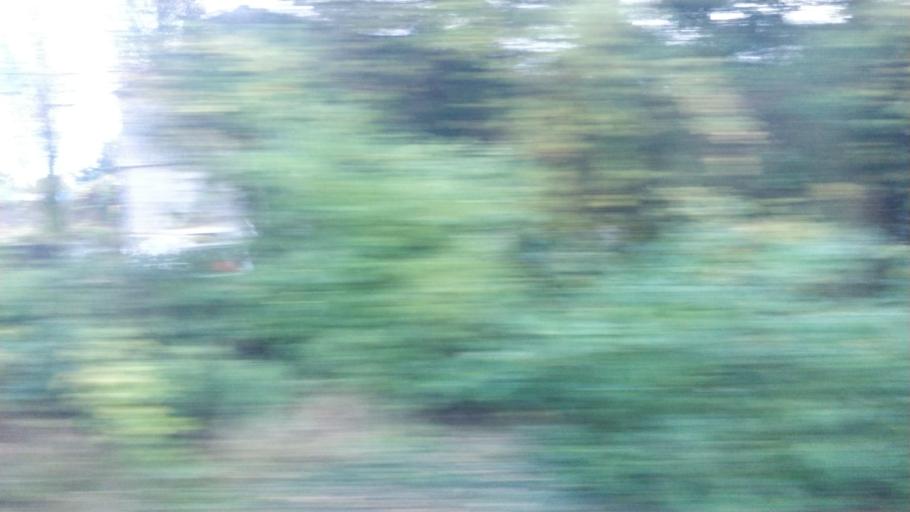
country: GB
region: England
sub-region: Lancashire
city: Ormskirk
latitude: 53.6111
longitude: -2.8658
